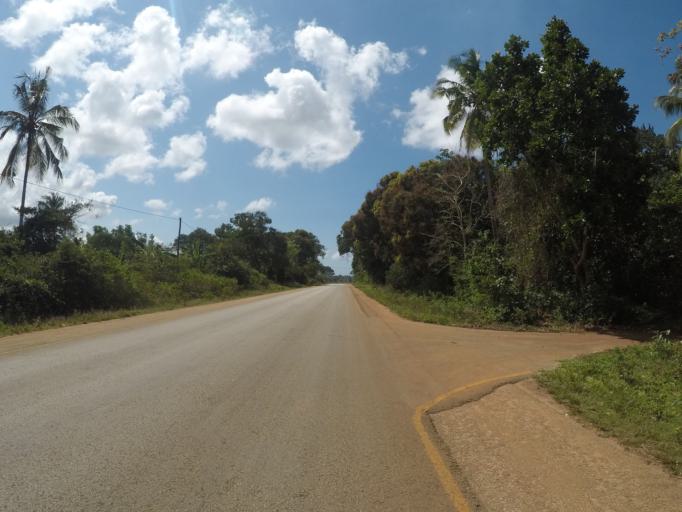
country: TZ
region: Zanzibar Central/South
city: Koani
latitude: -6.1667
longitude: 39.3303
